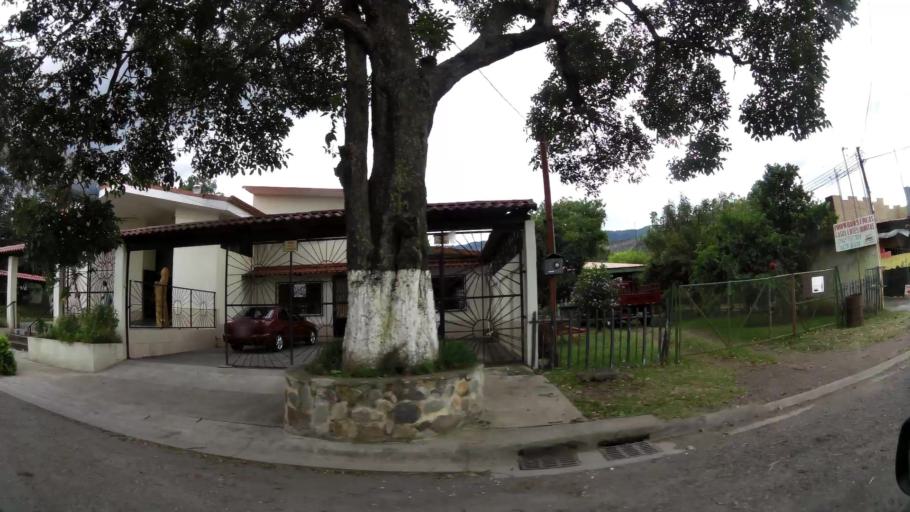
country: CR
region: San Jose
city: Santa Ana
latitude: 9.9339
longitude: -84.1865
